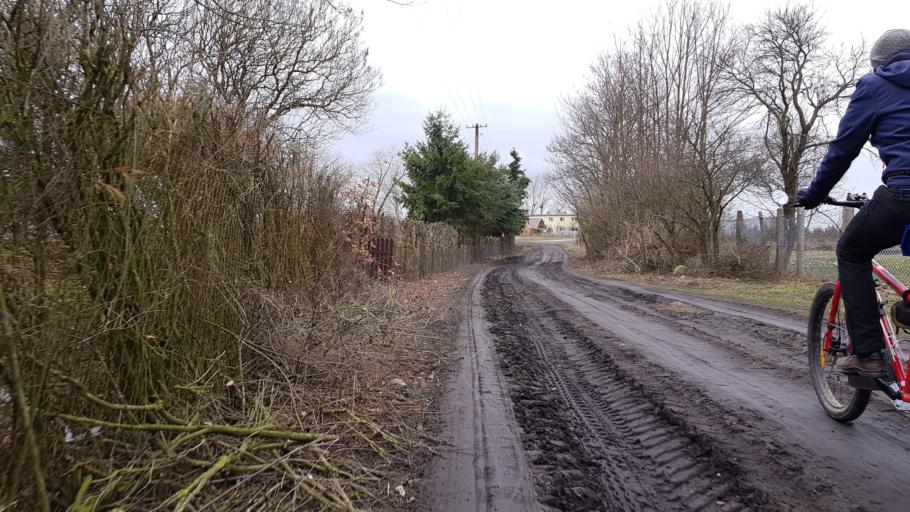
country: PL
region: West Pomeranian Voivodeship
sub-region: Powiat gryfinski
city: Banie
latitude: 53.0937
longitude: 14.7085
